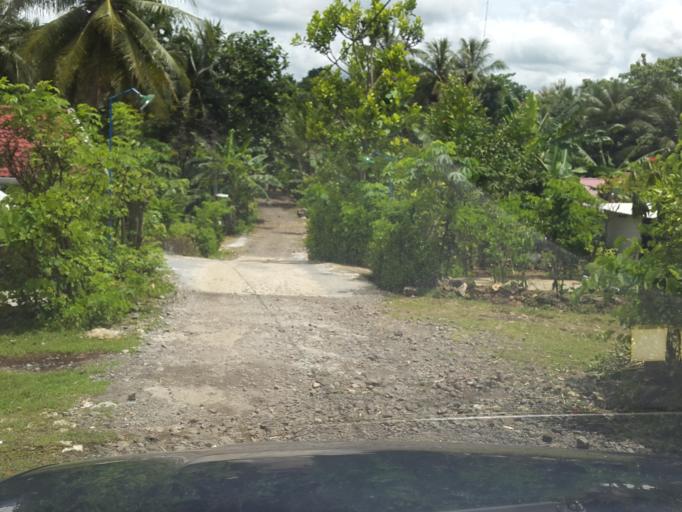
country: ID
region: Daerah Istimewa Yogyakarta
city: Wonosari
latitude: -7.9247
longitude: 110.6416
